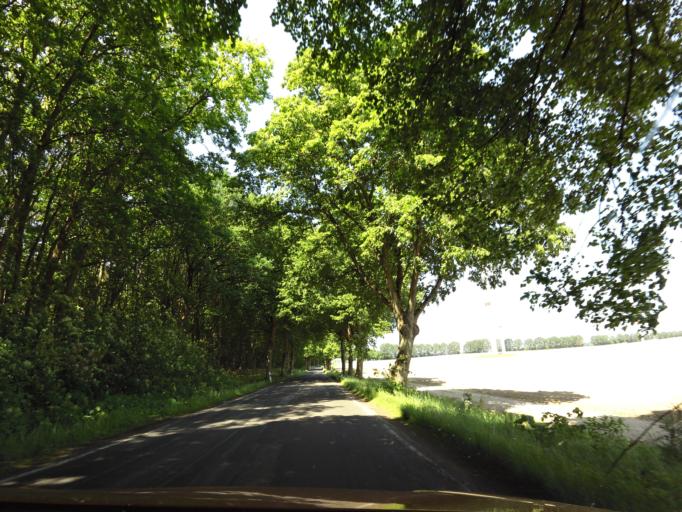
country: DE
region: Mecklenburg-Vorpommern
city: Neuburg
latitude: 53.4113
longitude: 11.8937
